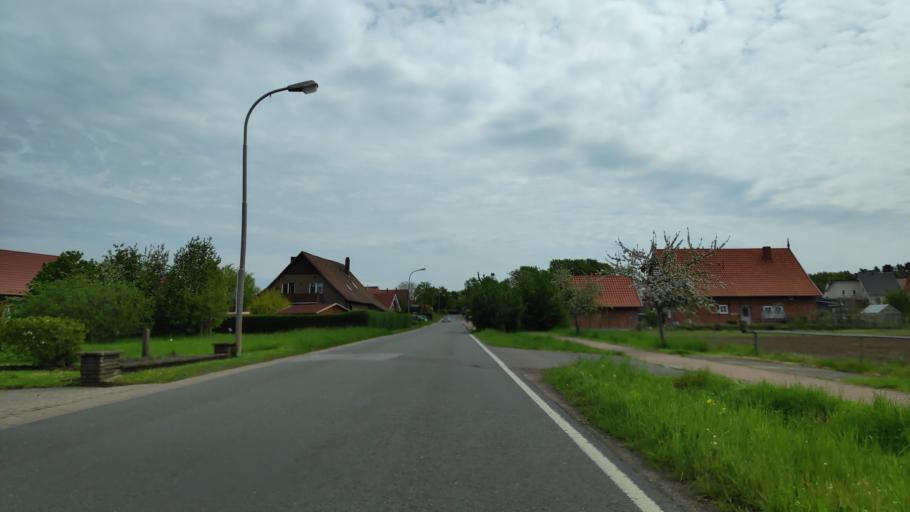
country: DE
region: North Rhine-Westphalia
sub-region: Regierungsbezirk Detmold
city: Petershagen
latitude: 52.3107
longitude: 8.9926
